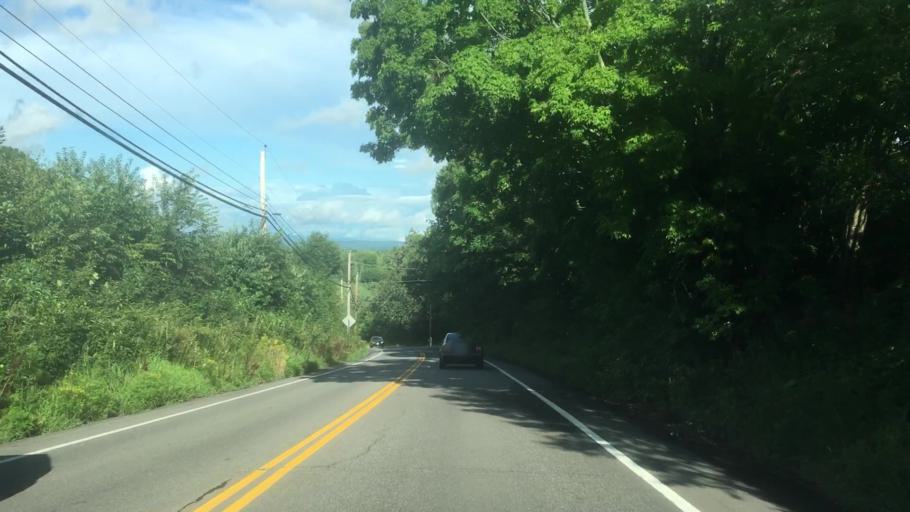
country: US
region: New Hampshire
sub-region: Merrimack County
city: Hopkinton
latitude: 43.1905
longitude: -71.6160
